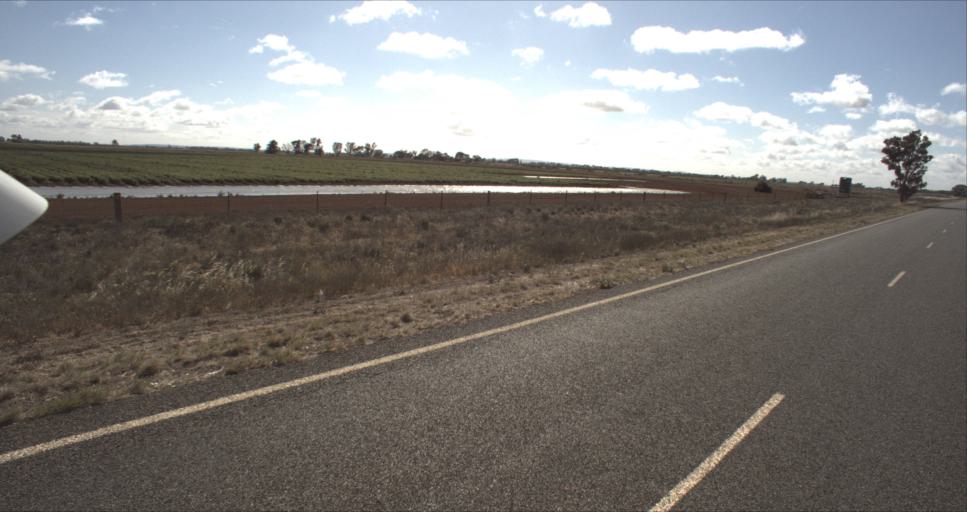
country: AU
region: New South Wales
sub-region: Leeton
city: Leeton
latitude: -34.5456
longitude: 146.2579
